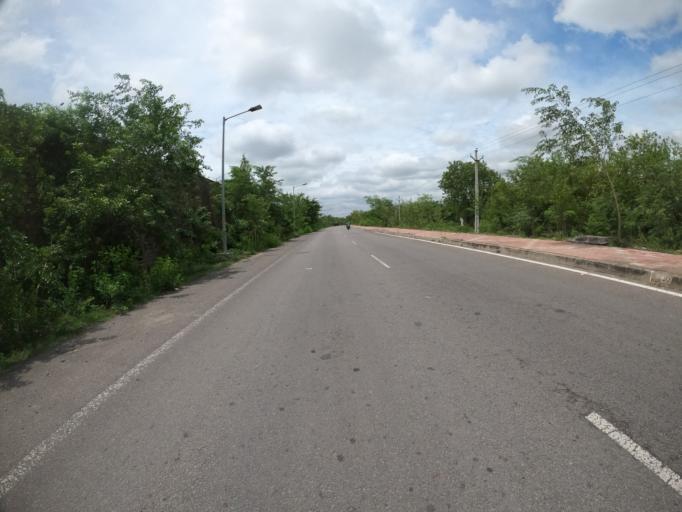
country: IN
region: Telangana
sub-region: Rangareddi
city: Balapur
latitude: 17.2810
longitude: 78.3825
